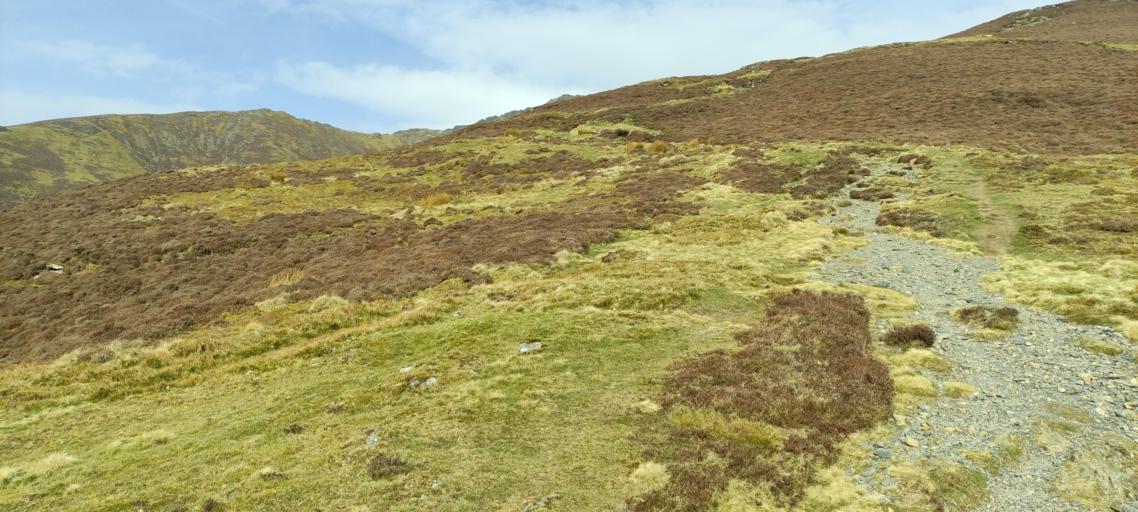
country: GB
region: England
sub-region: Cumbria
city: Keswick
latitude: 54.6305
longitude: -3.0437
